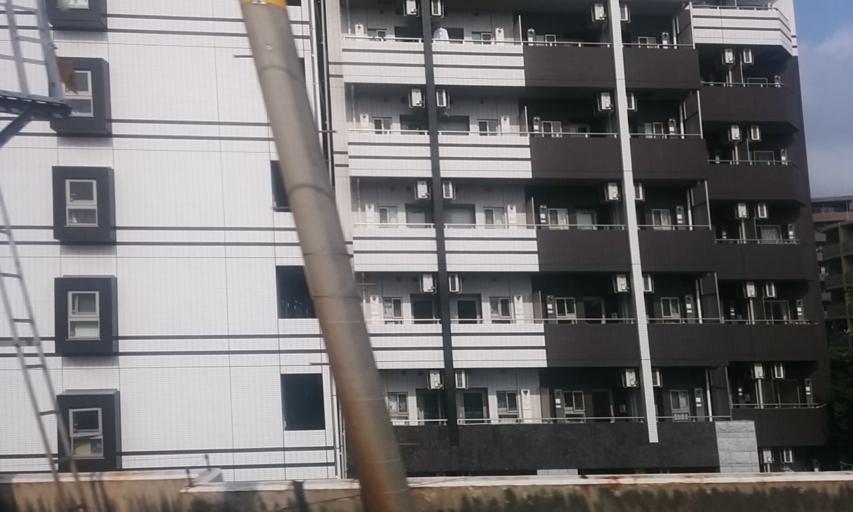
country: JP
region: Kanagawa
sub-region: Kawasaki-shi
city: Kawasaki
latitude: 35.5923
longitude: 139.7361
